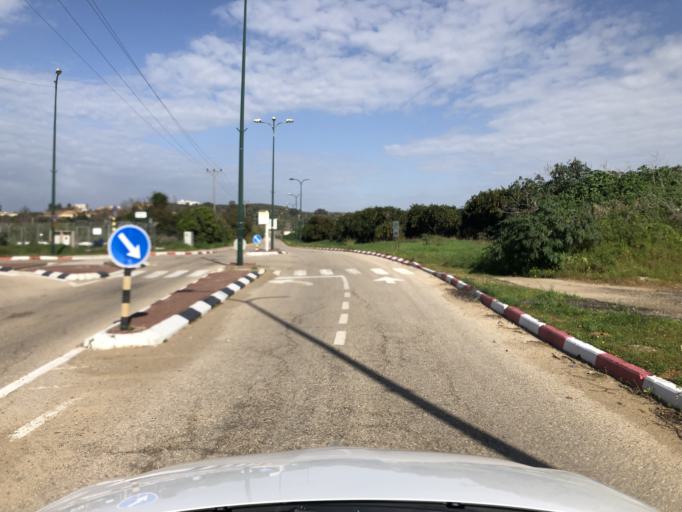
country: IL
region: Central District
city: Ness Ziona
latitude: 31.9157
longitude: 34.7788
